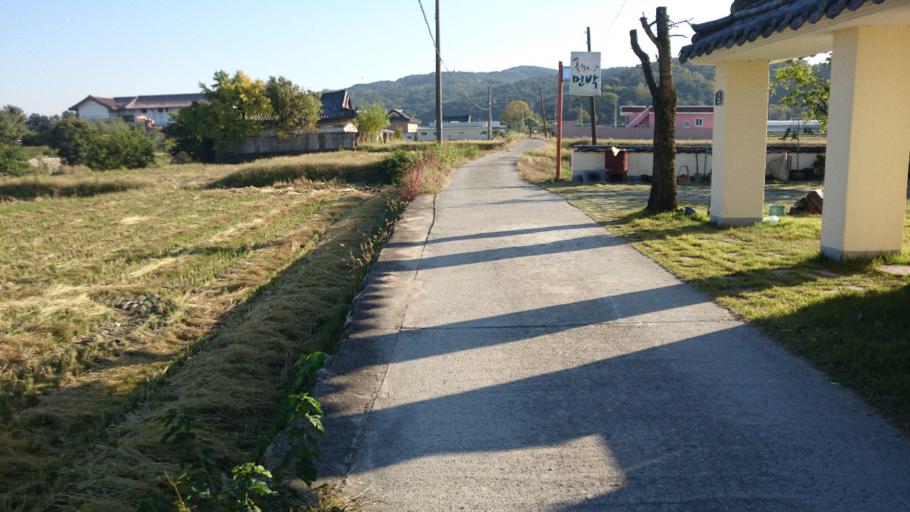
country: KR
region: Gyeongsangbuk-do
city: Kyonju
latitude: 35.8293
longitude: 129.2253
